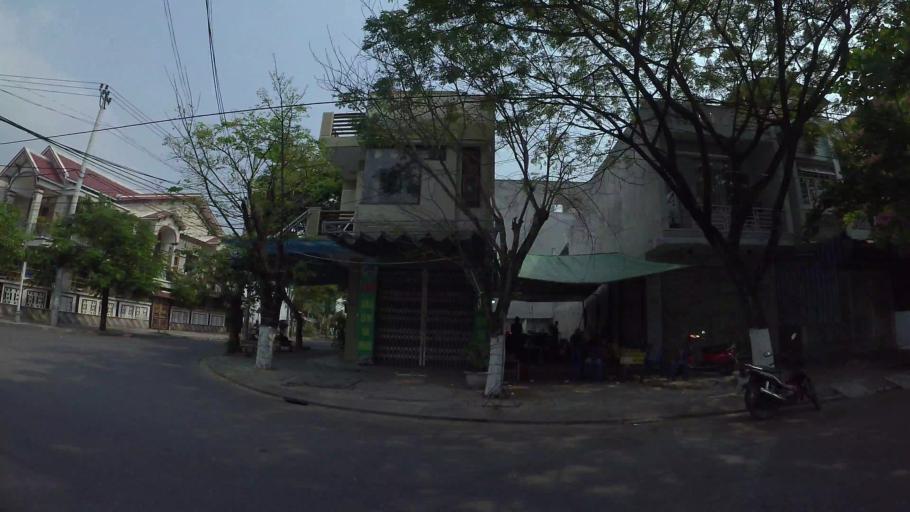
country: VN
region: Da Nang
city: Da Nang
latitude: 16.0948
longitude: 108.2302
